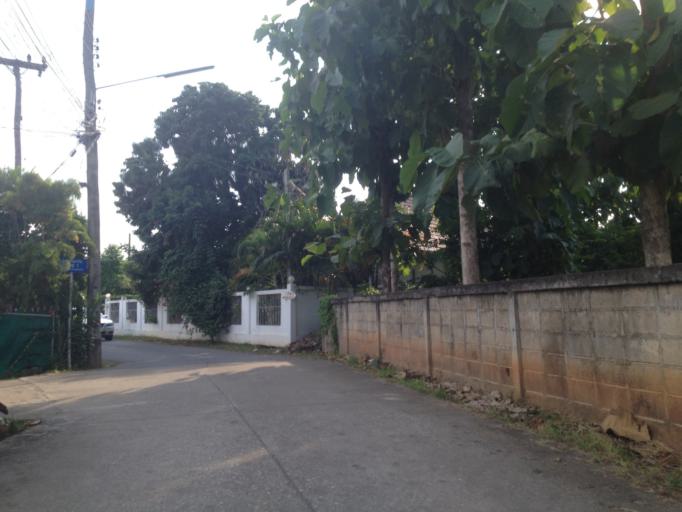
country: TH
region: Chiang Mai
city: Hang Dong
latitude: 18.7242
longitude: 98.9238
